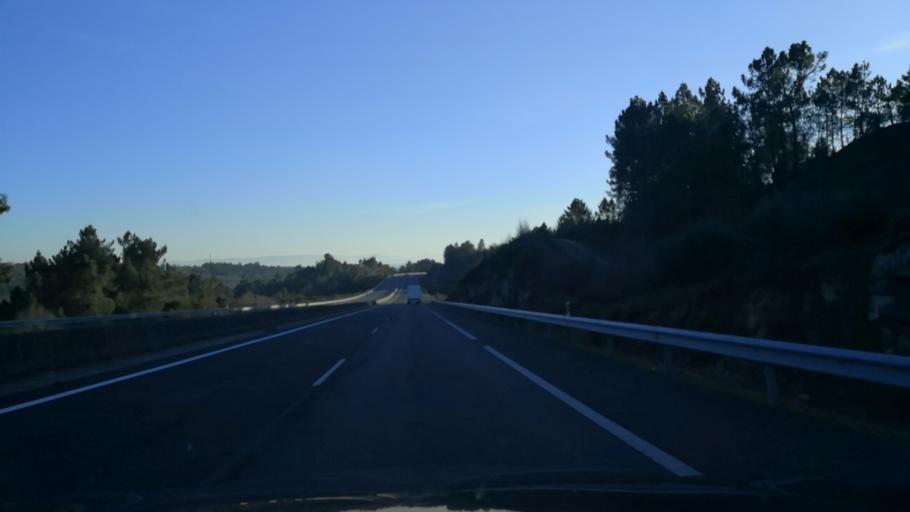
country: ES
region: Galicia
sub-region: Provincia de Ourense
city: Pinor
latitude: 42.5116
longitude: -8.0215
